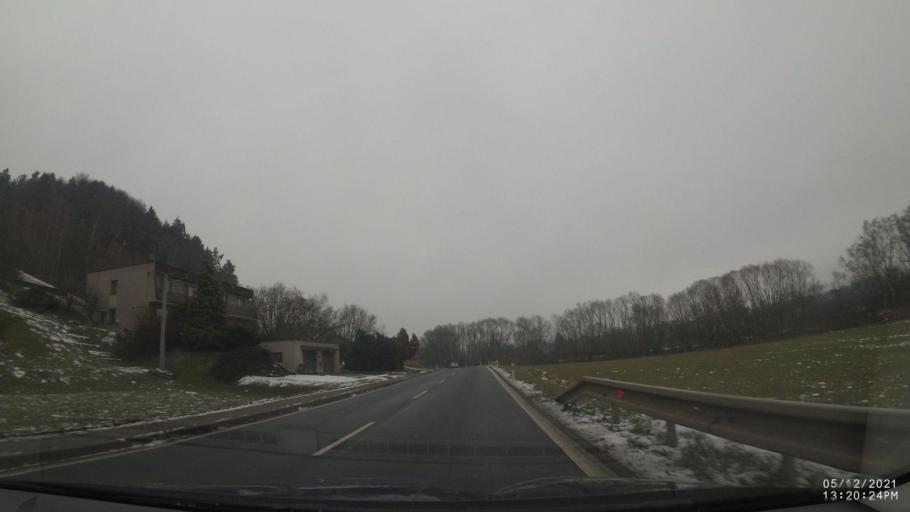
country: CZ
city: Velke Porici
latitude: 50.4498
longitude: 16.1885
